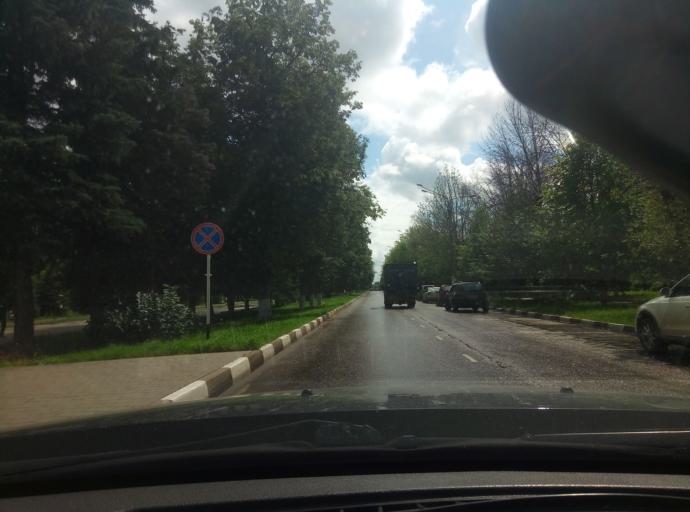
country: RU
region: Tula
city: Novomoskovsk
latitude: 54.0107
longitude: 38.2961
